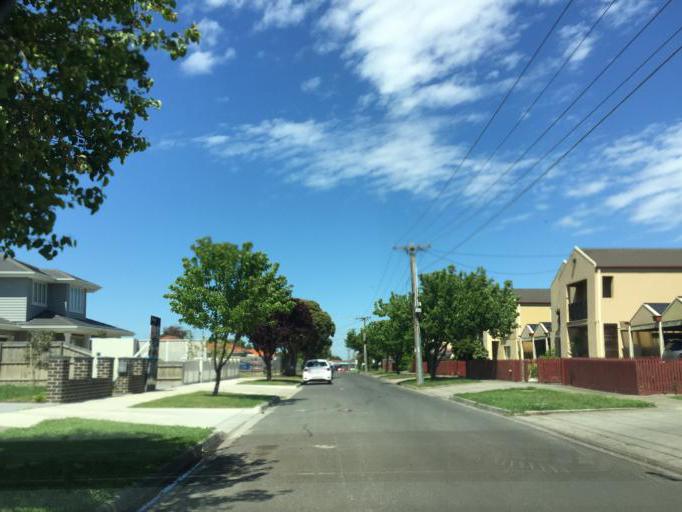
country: AU
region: Victoria
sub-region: Maribyrnong
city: Braybrook
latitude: -37.7886
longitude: 144.8468
